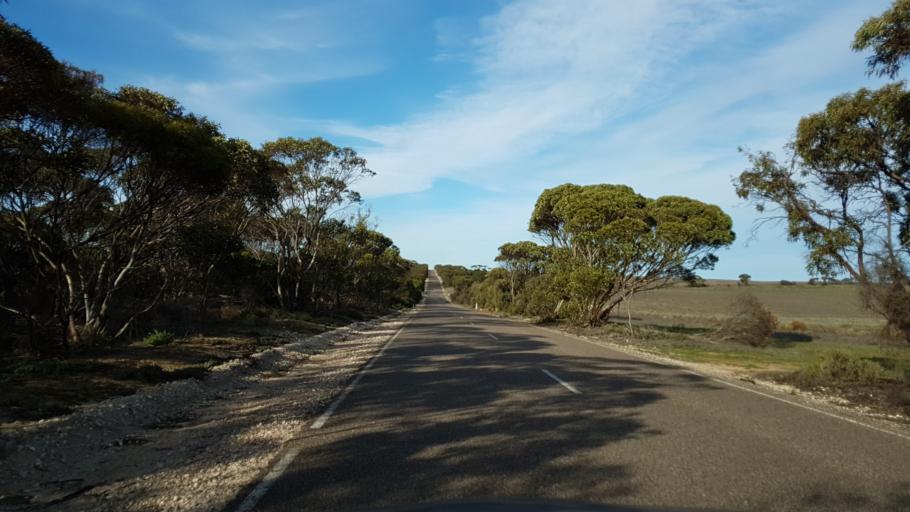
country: AU
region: South Australia
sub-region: Murray Bridge
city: Tailem Bend
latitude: -35.0649
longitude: 139.4654
